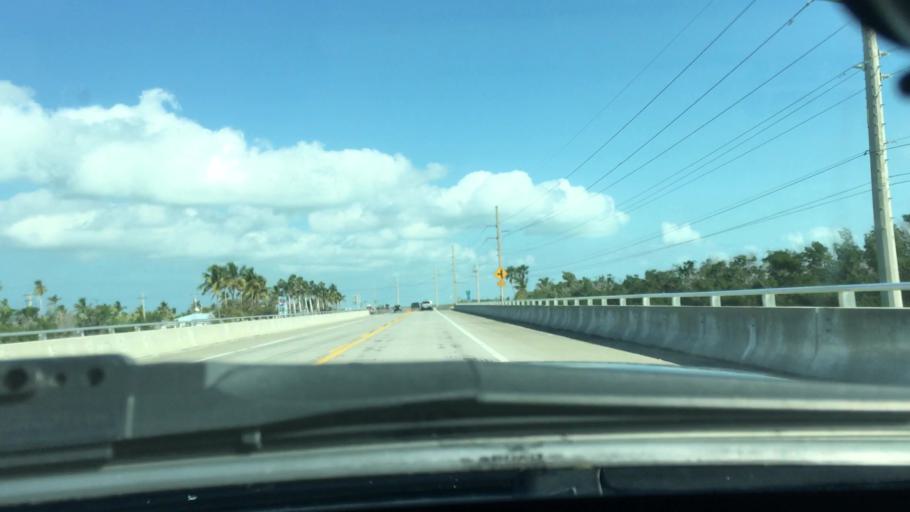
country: US
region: Florida
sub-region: Monroe County
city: Big Pine Key
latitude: 24.6706
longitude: -81.2492
